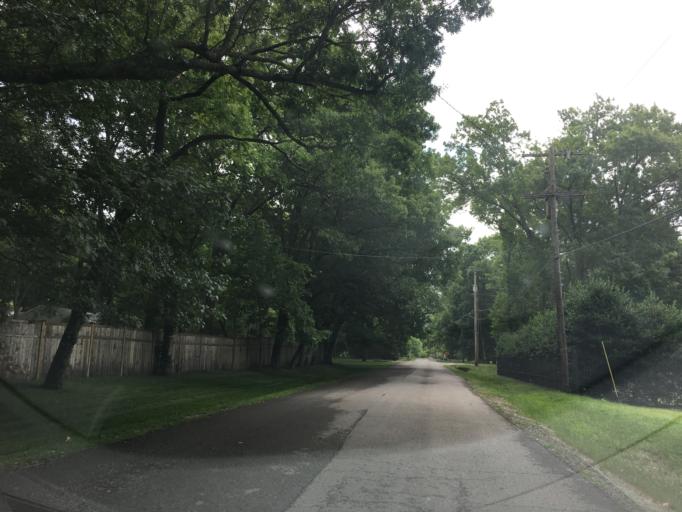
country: US
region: Tennessee
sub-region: Davidson County
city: Belle Meade
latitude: 36.0970
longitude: -86.8464
